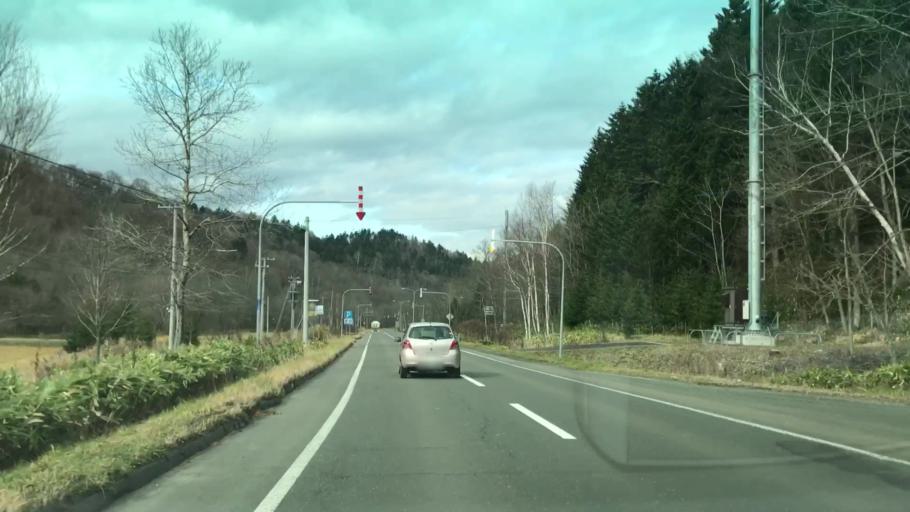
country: JP
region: Hokkaido
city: Shimo-furano
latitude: 42.9268
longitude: 142.4451
